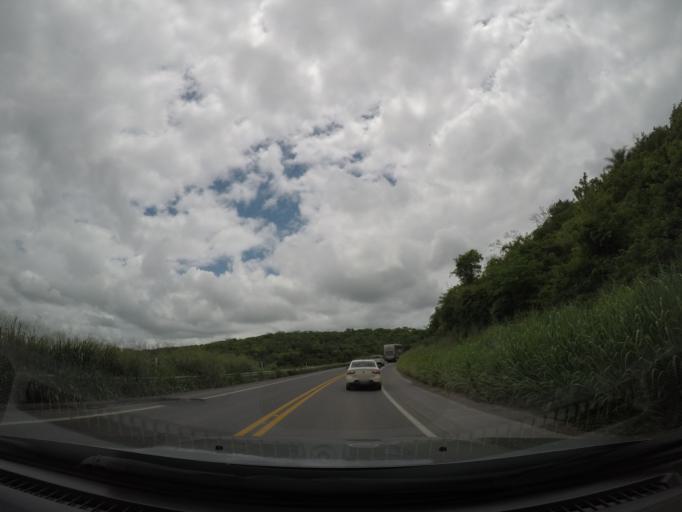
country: BR
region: Bahia
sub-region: Ruy Barbosa
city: Terra Nova
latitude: -12.4590
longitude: -40.5675
